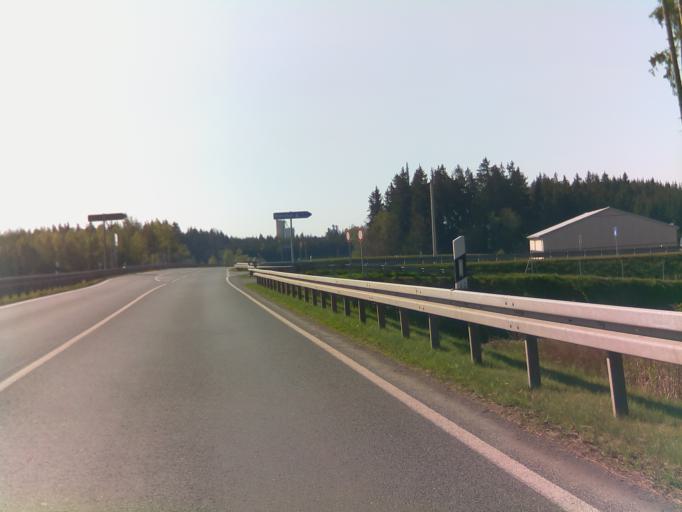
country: DE
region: Thuringia
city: Dittersdorf
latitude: 50.6586
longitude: 11.8111
